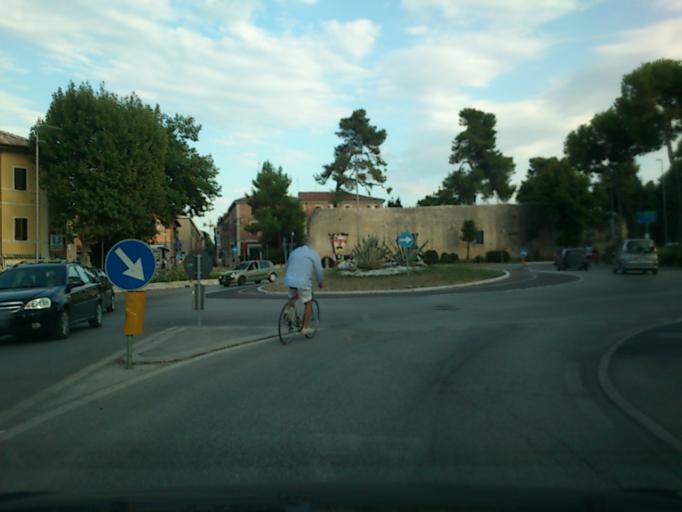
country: IT
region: The Marches
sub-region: Provincia di Pesaro e Urbino
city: Fano
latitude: 43.8466
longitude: 13.0123
